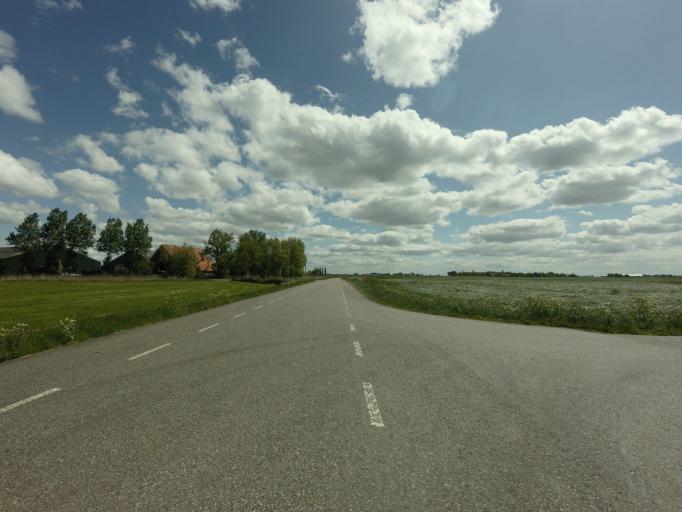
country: NL
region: Friesland
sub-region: Sudwest Fryslan
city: Makkum
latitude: 53.0919
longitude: 5.4121
